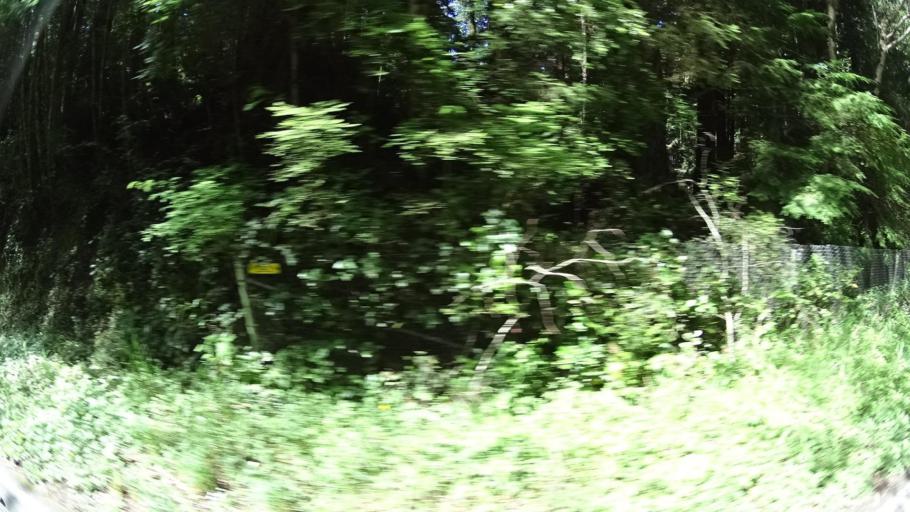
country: US
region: California
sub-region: Humboldt County
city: McKinleyville
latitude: 40.9703
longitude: -124.0602
